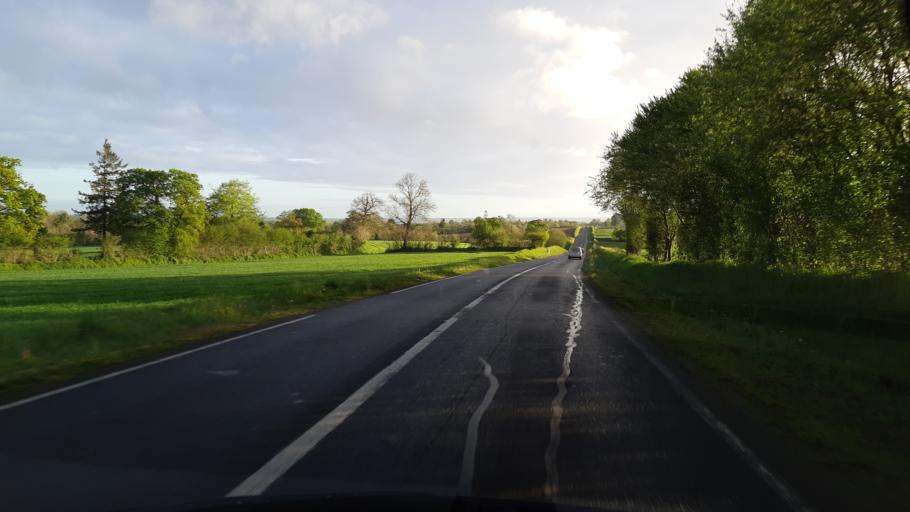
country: FR
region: Lower Normandy
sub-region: Departement de la Manche
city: Agneaux
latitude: 49.0332
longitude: -1.1352
